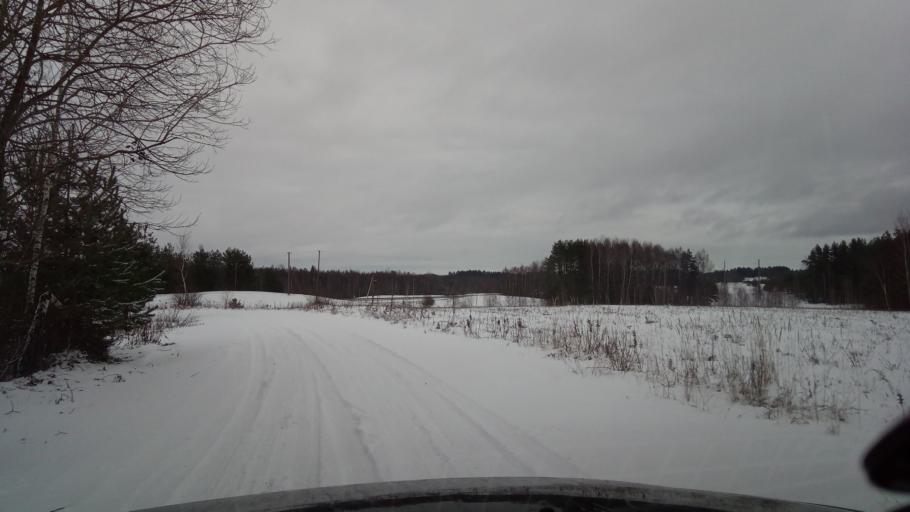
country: LT
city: Zarasai
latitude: 55.6706
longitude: 26.0923
